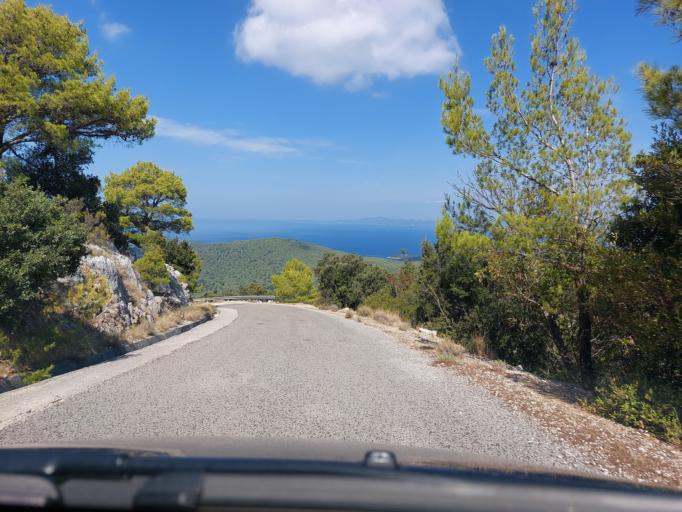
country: HR
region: Dubrovacko-Neretvanska
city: Smokvica
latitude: 42.7465
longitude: 16.8531
